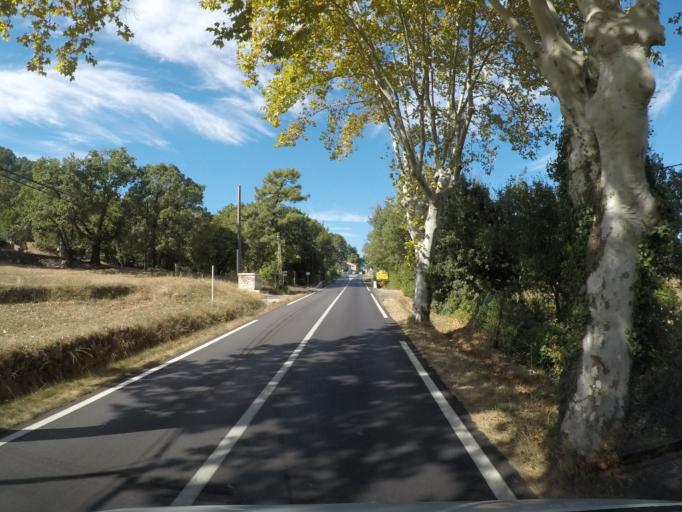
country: FR
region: Languedoc-Roussillon
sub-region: Departement du Gard
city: Anduze
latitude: 44.0693
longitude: 3.9698
